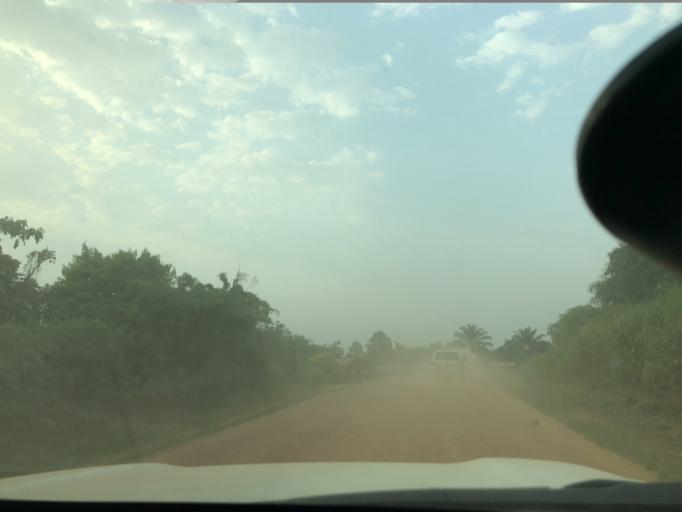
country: CD
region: Nord Kivu
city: Beni
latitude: 0.3459
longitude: 29.6545
